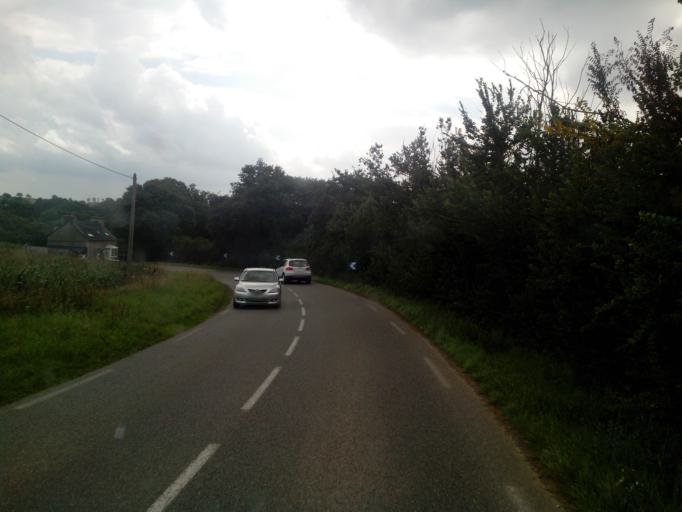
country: FR
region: Brittany
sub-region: Departement des Cotes-d'Armor
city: Plouezec
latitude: 48.7158
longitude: -2.9753
